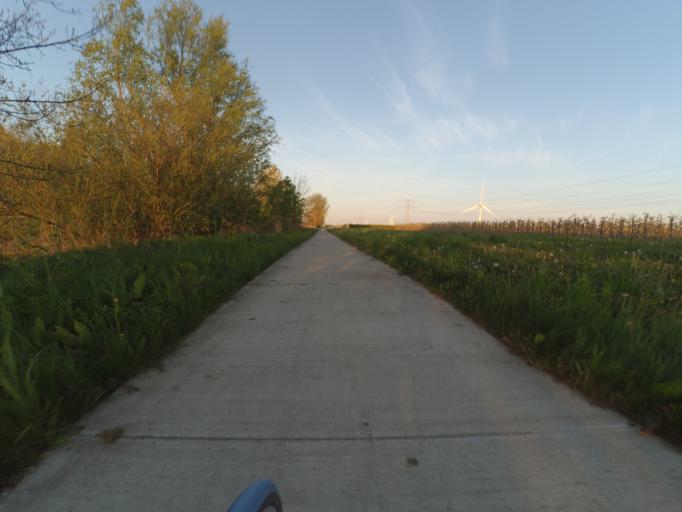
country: NL
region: Flevoland
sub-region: Gemeente Zeewolde
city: Zeewolde
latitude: 52.3544
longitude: 5.4842
